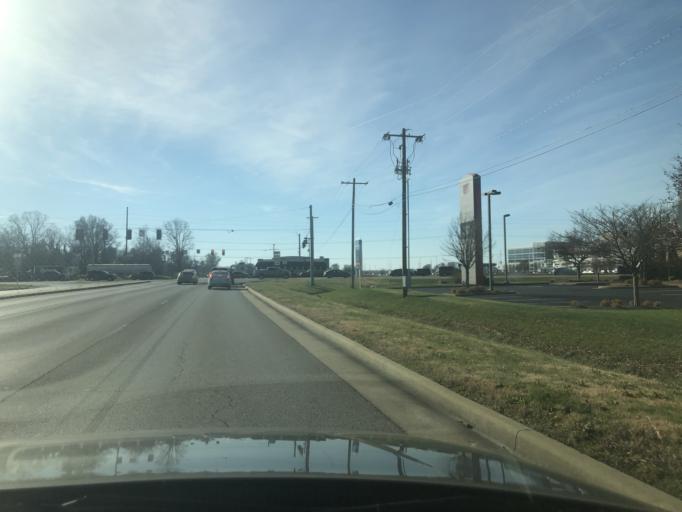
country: US
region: Indiana
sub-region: Warrick County
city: Newburgh
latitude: 37.9777
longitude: -87.4413
